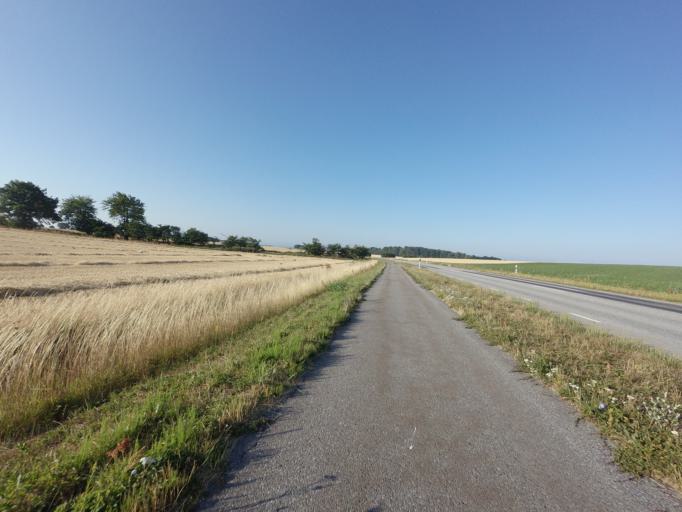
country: SE
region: Skane
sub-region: Helsingborg
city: Glumslov
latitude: 55.9245
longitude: 12.8172
